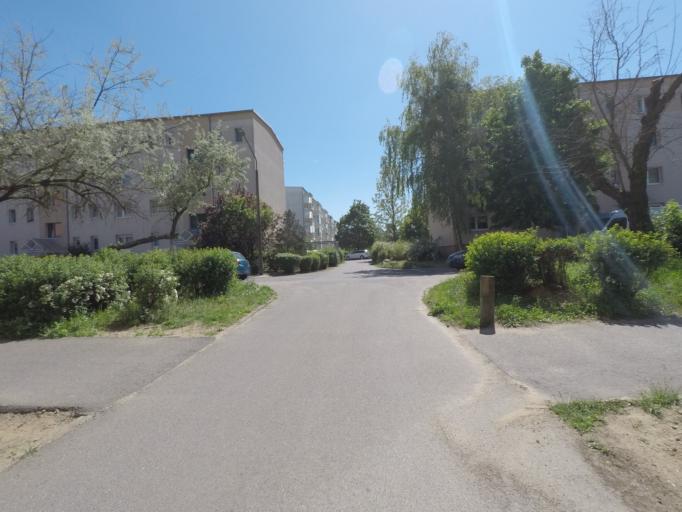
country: DE
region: Brandenburg
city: Melchow
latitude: 52.8359
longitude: 13.7380
